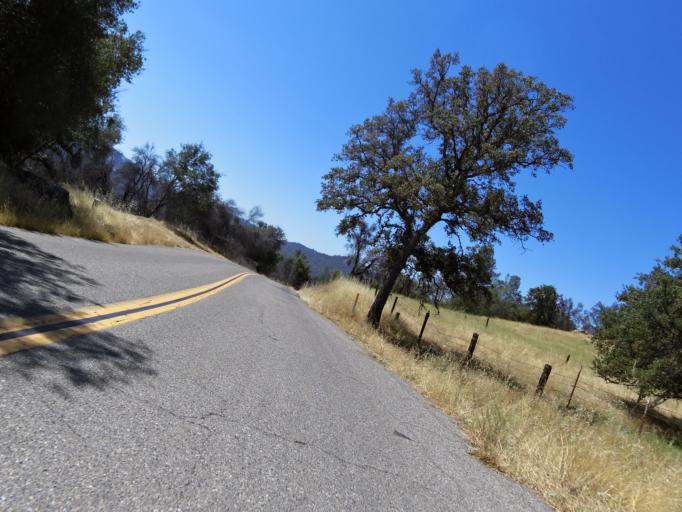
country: US
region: California
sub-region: Fresno County
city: Auberry
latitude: 37.1710
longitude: -119.5152
